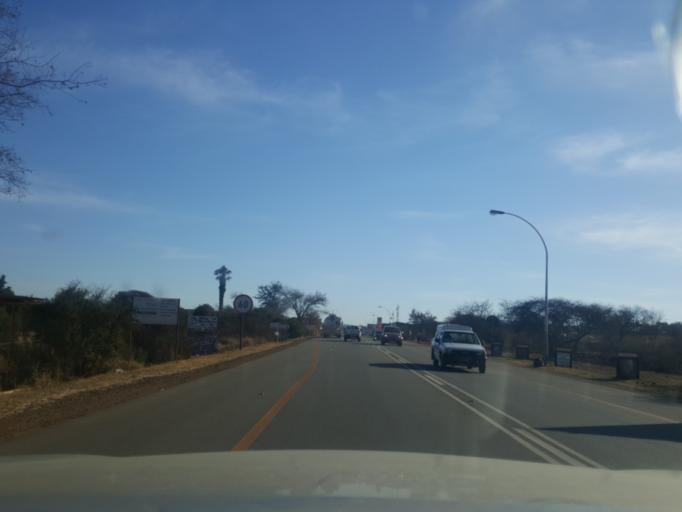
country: ZA
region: North-West
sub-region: Ngaka Modiri Molema District Municipality
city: Zeerust
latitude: -25.5428
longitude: 26.0893
